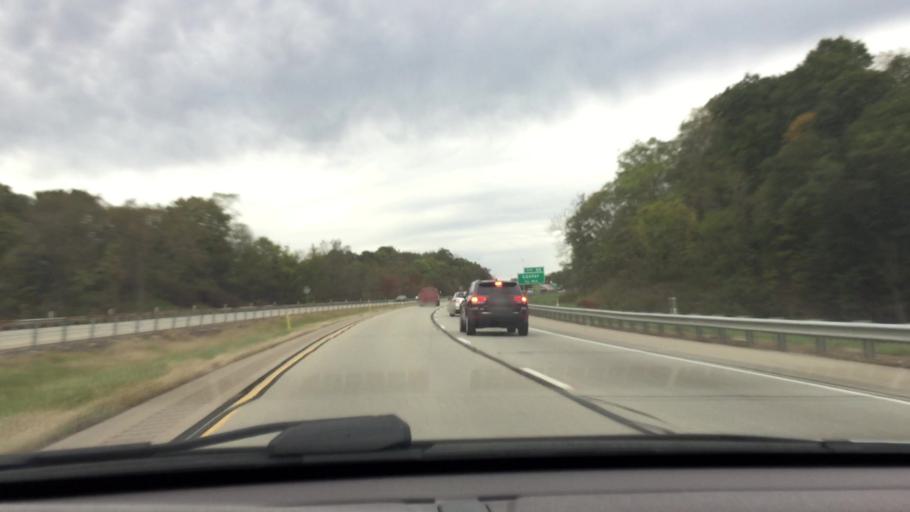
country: US
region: Pennsylvania
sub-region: Beaver County
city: Beaver
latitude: 40.6275
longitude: -80.3248
